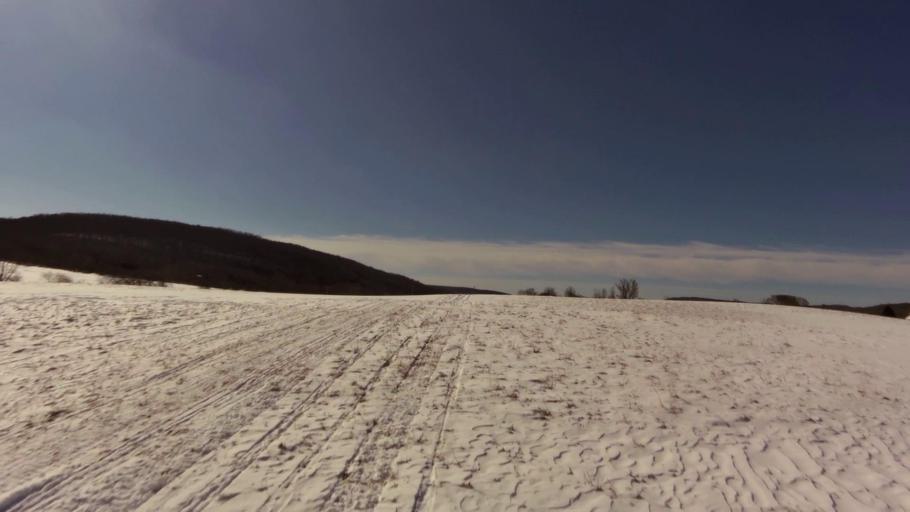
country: US
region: New York
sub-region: Allegany County
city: Cuba
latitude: 42.3349
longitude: -78.3060
